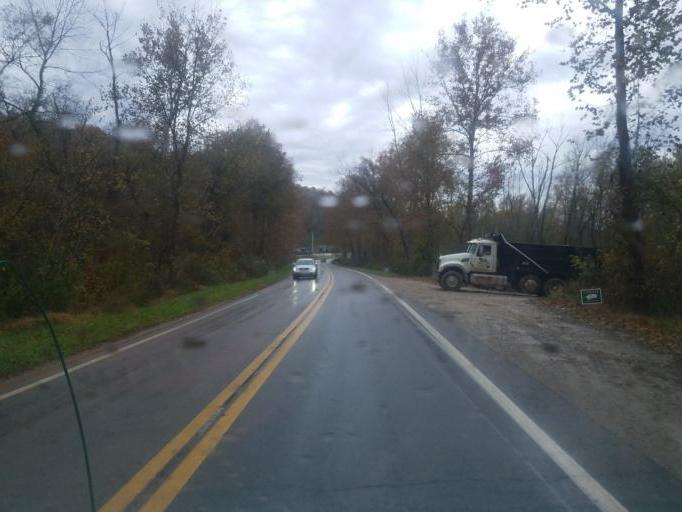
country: US
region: West Virginia
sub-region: Wood County
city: Williamstown
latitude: 39.3896
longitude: -81.4737
